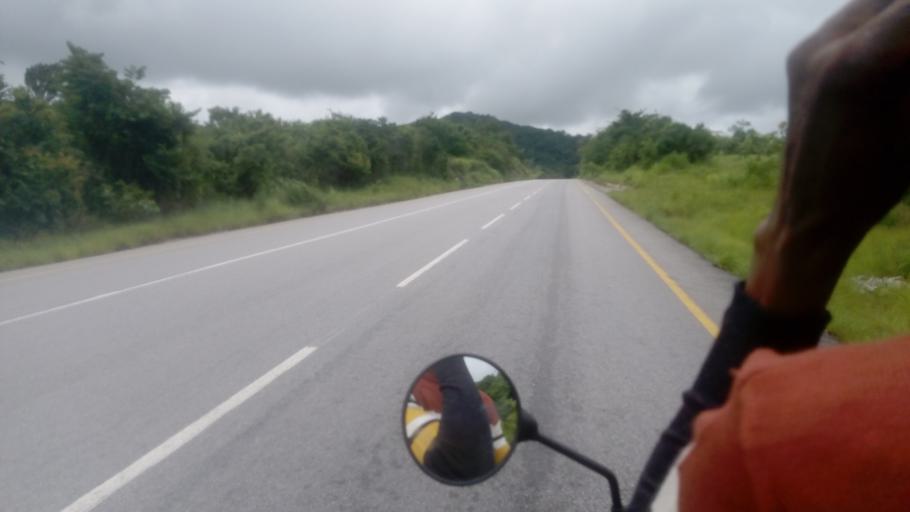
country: SL
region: Northern Province
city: Masaka
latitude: 8.6609
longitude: -11.7877
